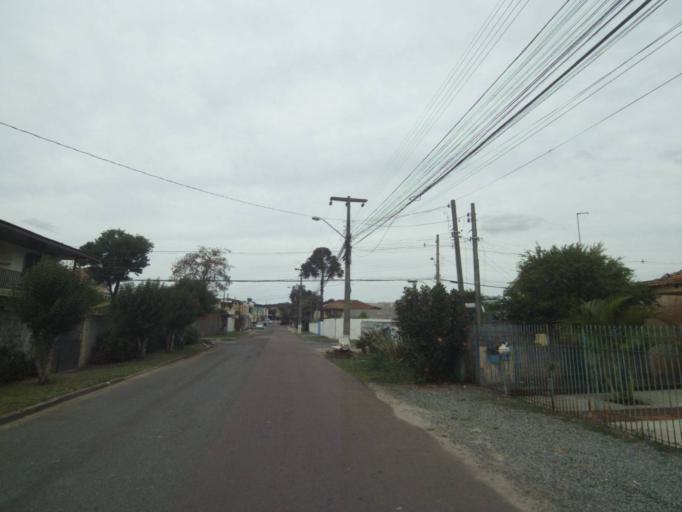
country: BR
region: Parana
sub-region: Curitiba
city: Curitiba
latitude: -25.5140
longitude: -49.3321
